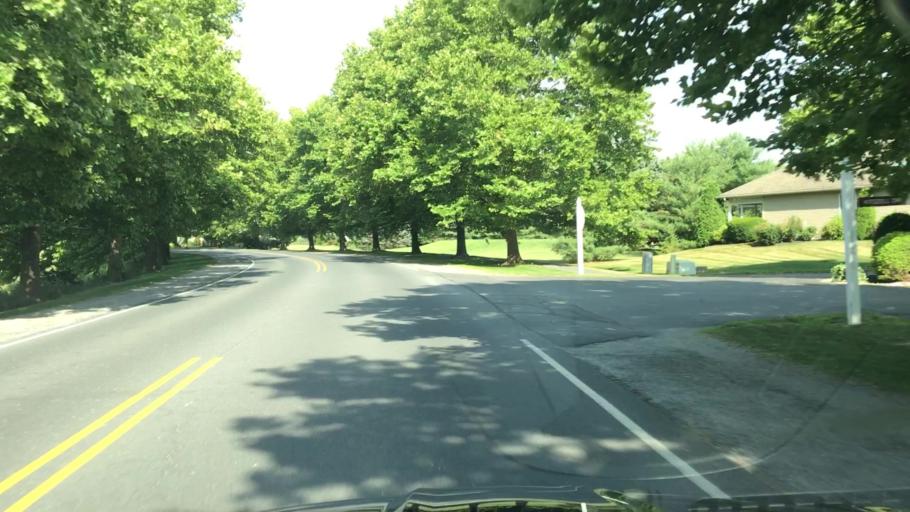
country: US
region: Pennsylvania
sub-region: Cumberland County
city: Boiling Springs
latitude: 40.1819
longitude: -77.1467
